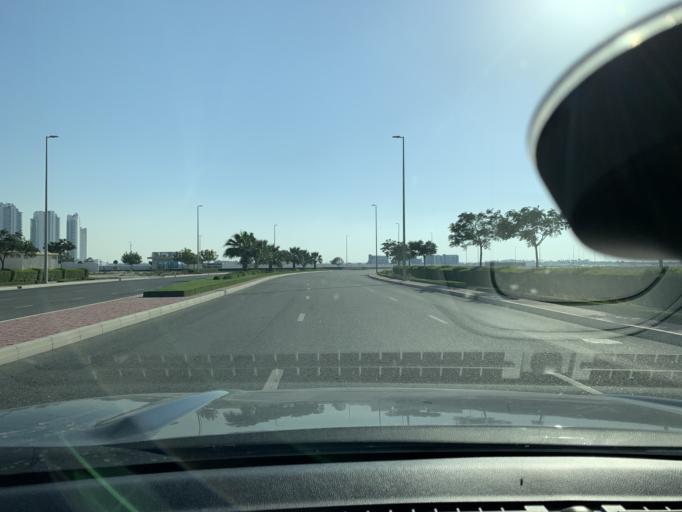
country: AE
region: Dubai
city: Dubai
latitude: 25.0368
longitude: 55.2441
